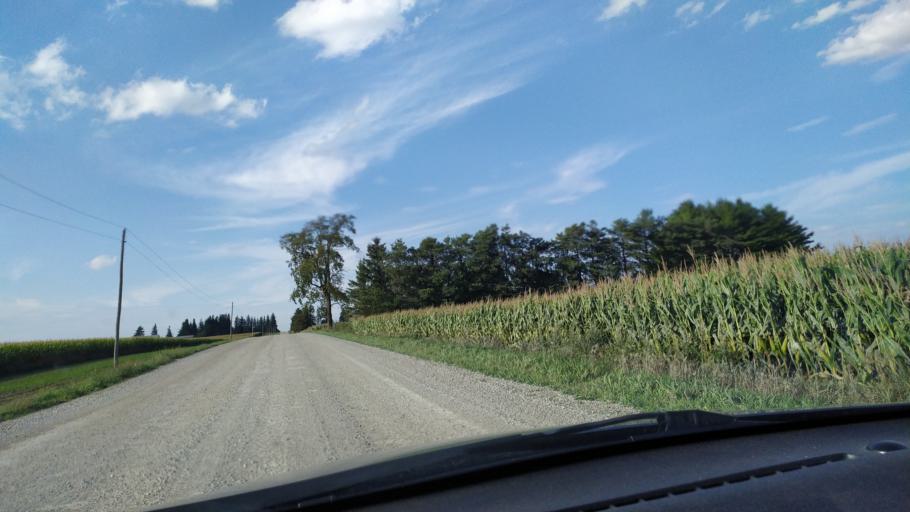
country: CA
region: Ontario
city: Stratford
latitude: 43.2752
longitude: -80.9422
